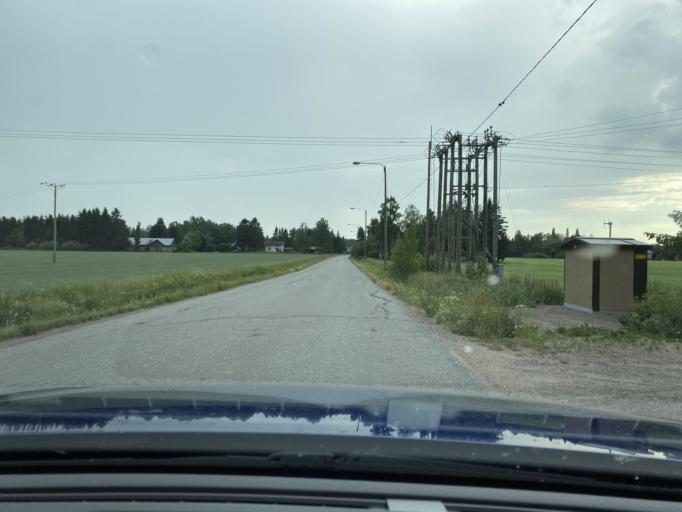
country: FI
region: Satakunta
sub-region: Rauma
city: Eura
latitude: 61.1448
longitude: 22.1243
